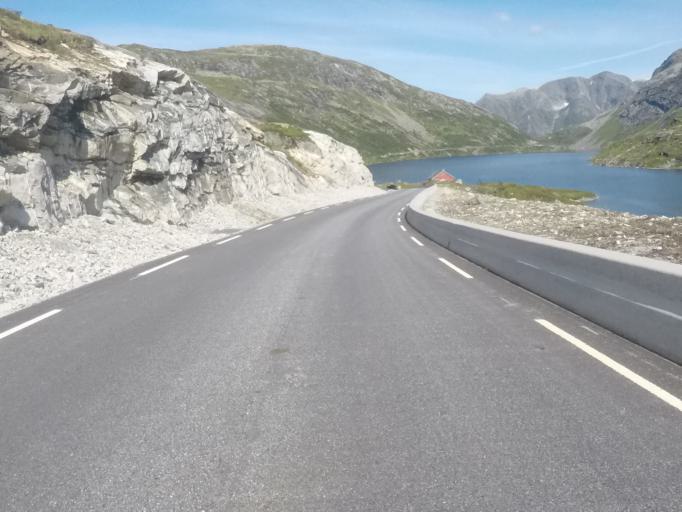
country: NO
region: Sogn og Fjordane
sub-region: Balestrand
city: Balestrand
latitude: 61.3435
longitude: 6.4625
